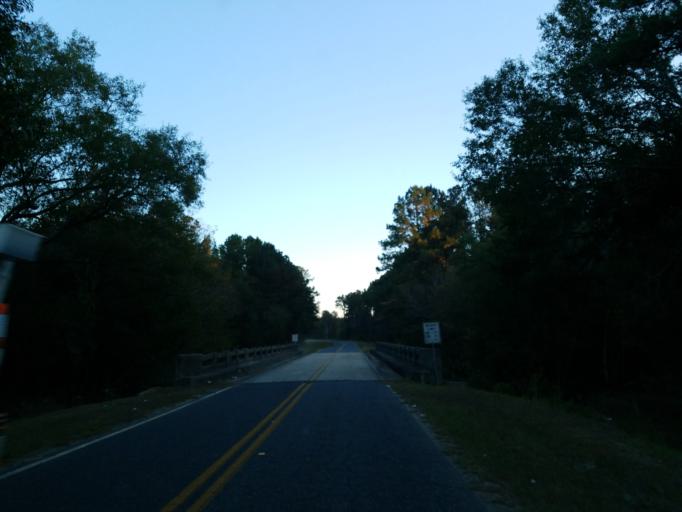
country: US
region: Georgia
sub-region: Ben Hill County
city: Fitzgerald
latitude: 31.6822
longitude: -83.4085
